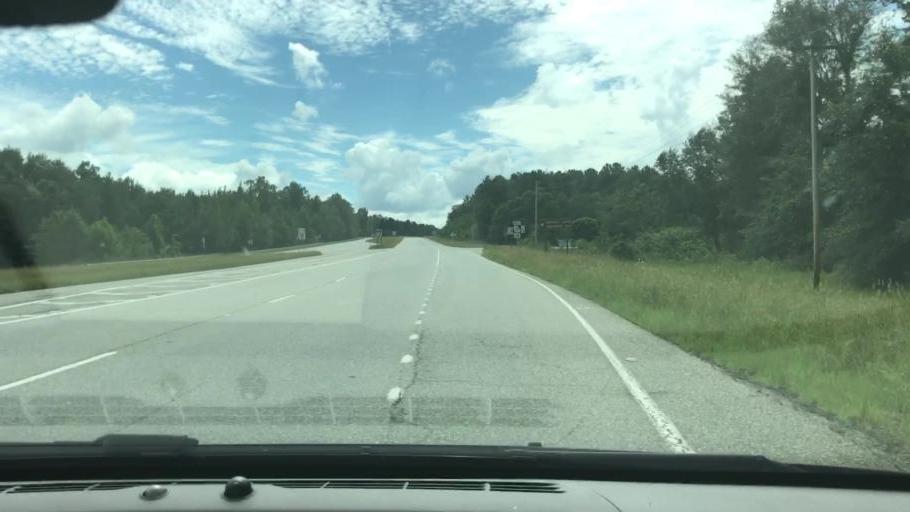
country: US
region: Georgia
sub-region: Stewart County
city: Lumpkin
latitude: 32.1474
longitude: -84.8256
